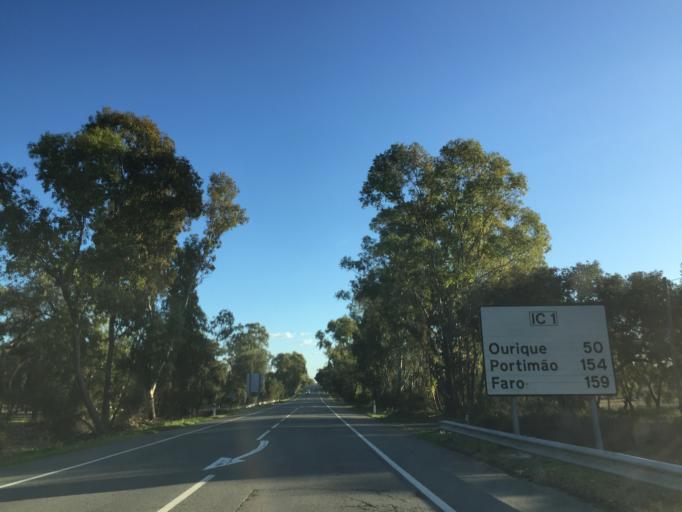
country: PT
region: Setubal
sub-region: Grandola
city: Grandola
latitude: 38.0326
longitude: -8.4003
